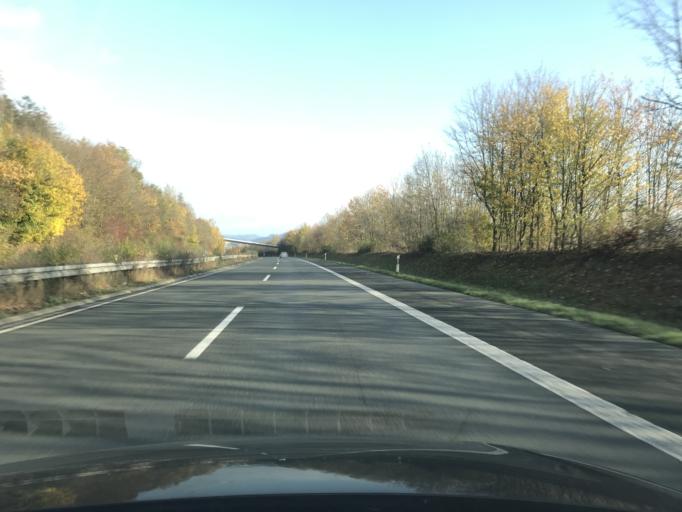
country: DE
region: North Rhine-Westphalia
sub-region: Regierungsbezirk Arnsberg
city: Meschede
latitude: 51.3567
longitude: 8.2176
